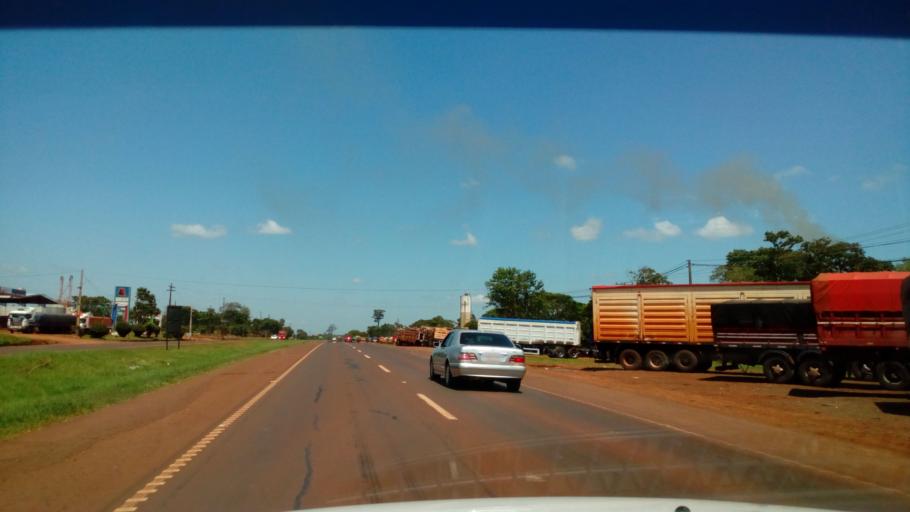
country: PY
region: Alto Parana
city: Colonia Yguazu
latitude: -25.4853
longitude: -54.8801
